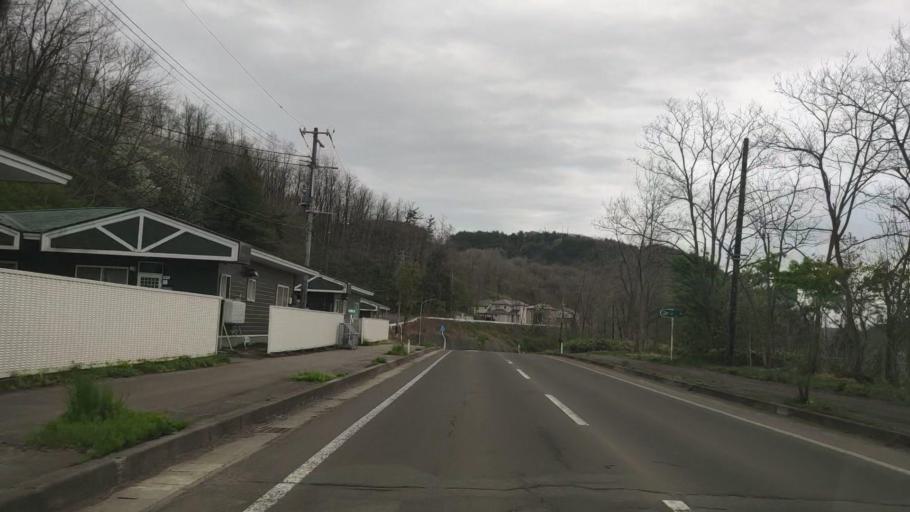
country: JP
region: Akita
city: Hanawa
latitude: 40.3275
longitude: 140.7477
